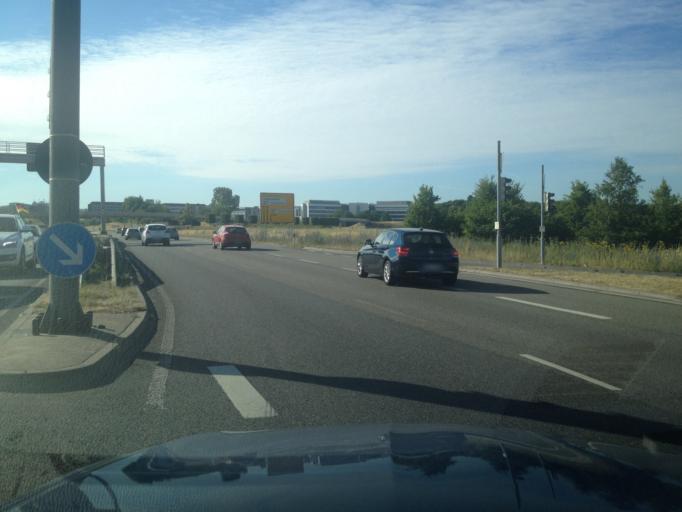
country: DE
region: Baden-Wuerttemberg
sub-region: Karlsruhe Region
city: Walldorf
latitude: 49.2993
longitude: 8.6327
